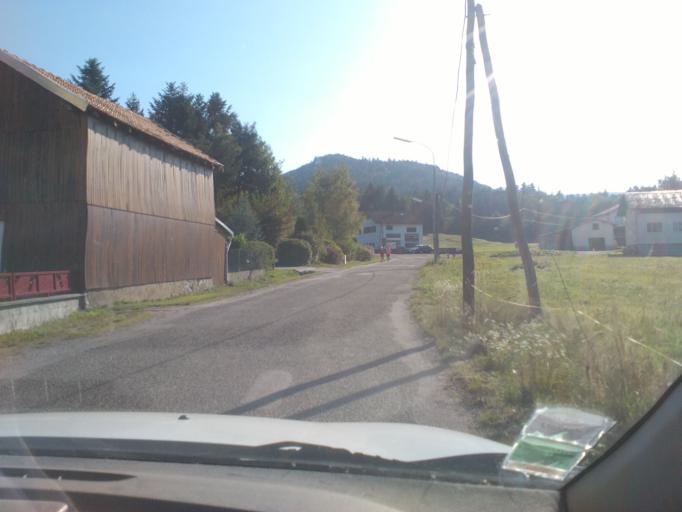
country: FR
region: Lorraine
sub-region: Departement des Vosges
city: Vagney
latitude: 48.0213
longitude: 6.7120
